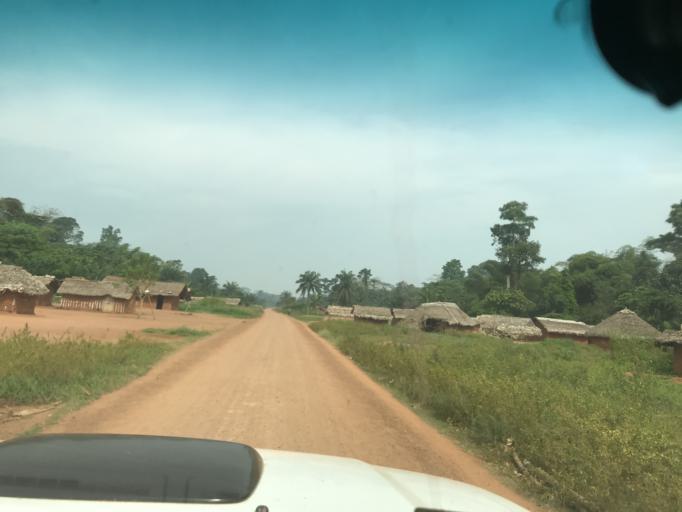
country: CD
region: Eastern Province
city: Buta
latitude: 2.8560
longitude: 24.5087
